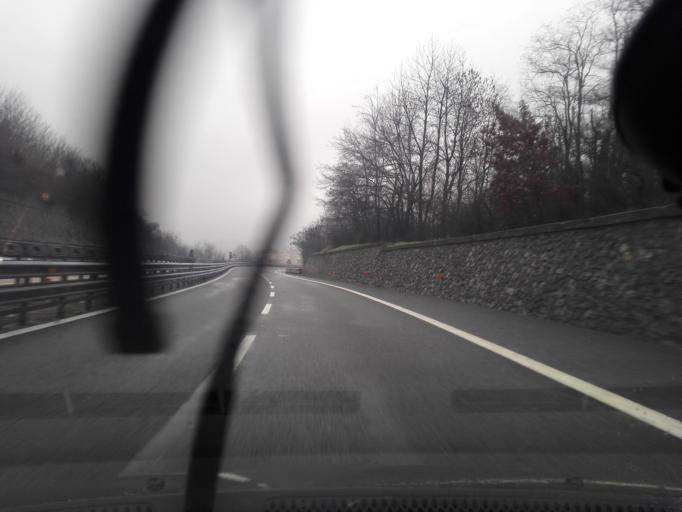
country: IT
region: Piedmont
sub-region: Provincia di Alessandria
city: Stazzano
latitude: 44.7107
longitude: 8.8712
